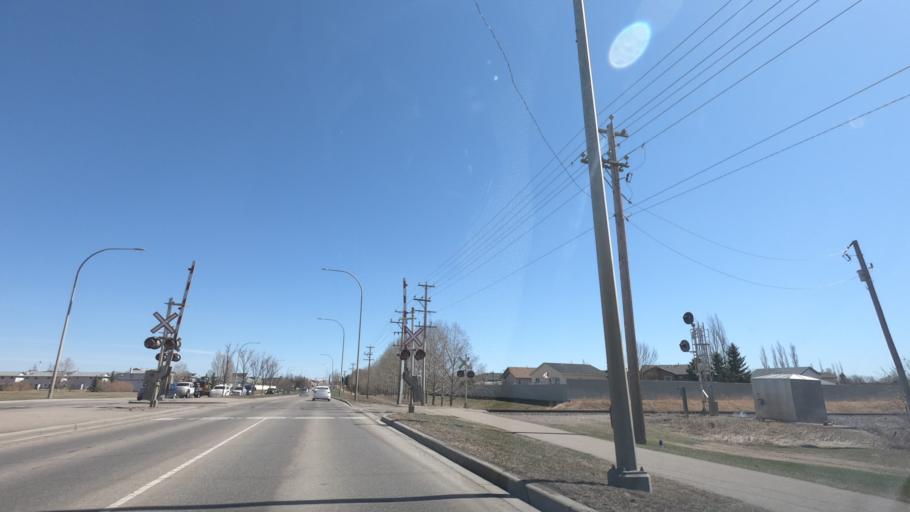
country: CA
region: Alberta
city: Airdrie
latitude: 51.2999
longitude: -114.0202
